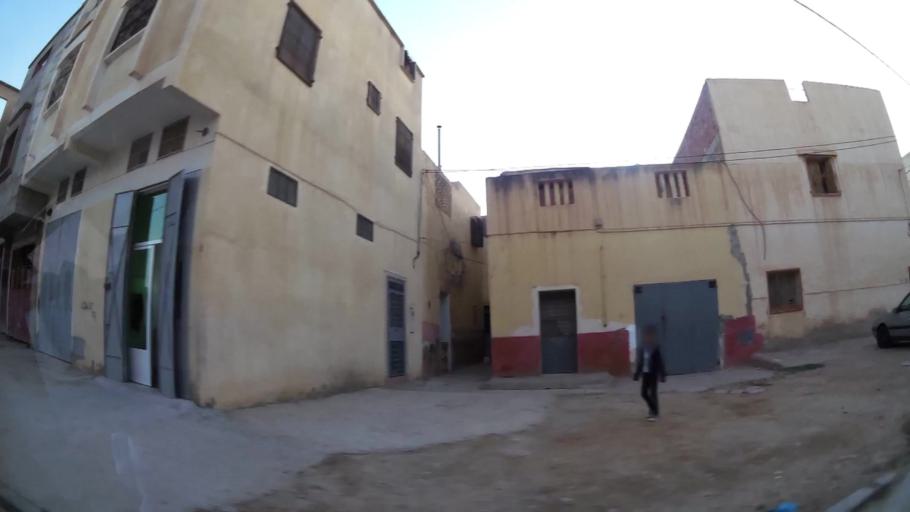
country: MA
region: Oriental
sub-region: Oujda-Angad
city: Oujda
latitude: 34.6982
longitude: -1.9217
